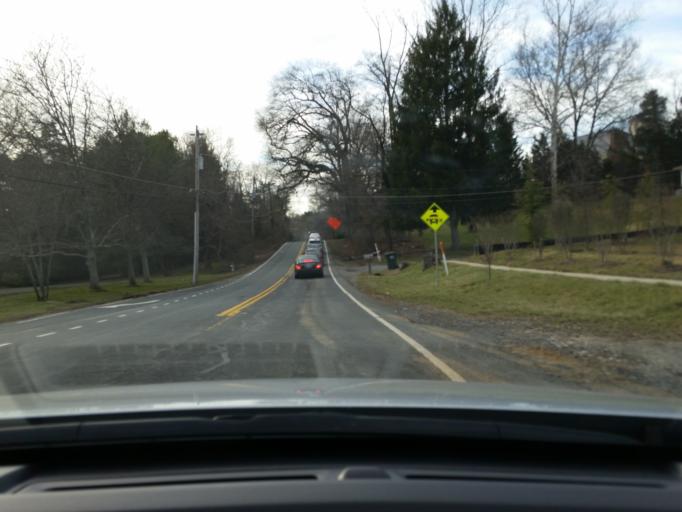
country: US
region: Virginia
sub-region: Fairfax County
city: McLean
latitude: 38.9511
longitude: -77.1789
